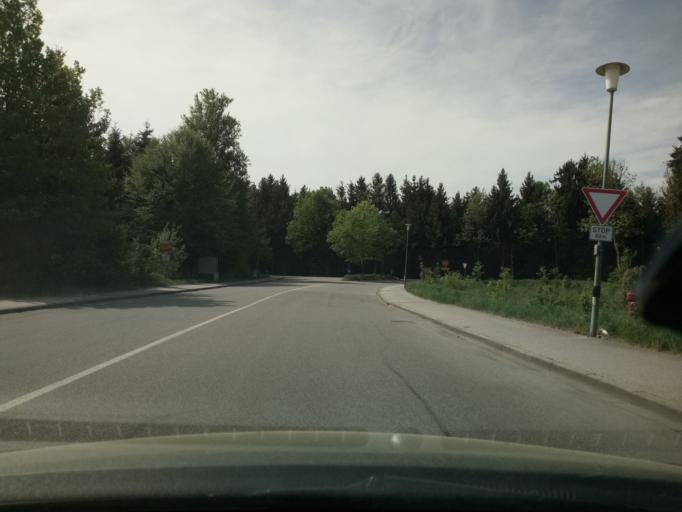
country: DE
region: Bavaria
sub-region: Upper Bavaria
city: Waldkraiburg
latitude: 48.1970
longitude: 12.3829
